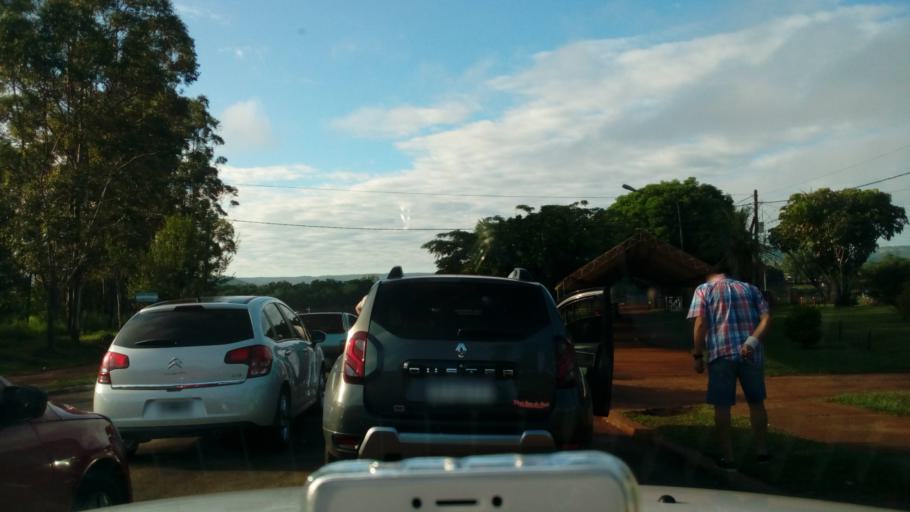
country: AR
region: Misiones
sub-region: Departamento de San Javier
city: San Javier
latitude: -27.8929
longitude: -55.1355
